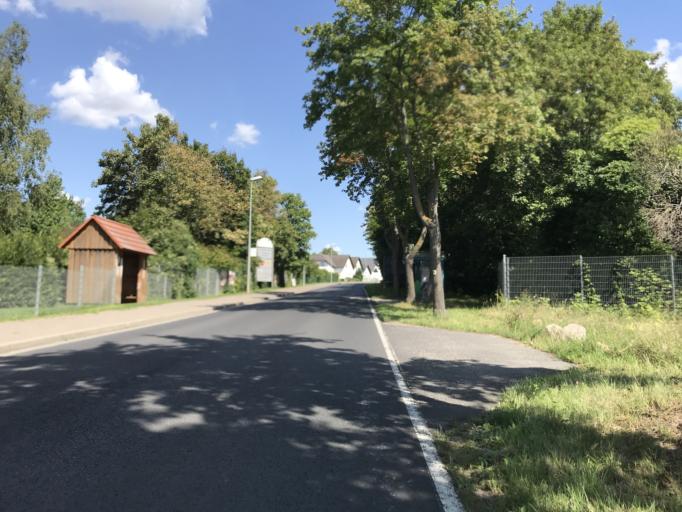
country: DE
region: Rheinland-Pfalz
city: Sprendlingen
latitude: 49.8605
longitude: 7.9950
